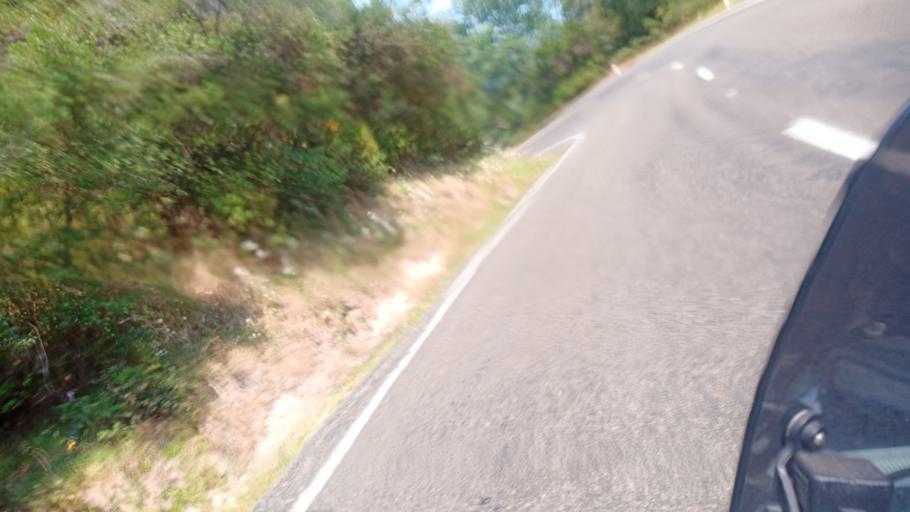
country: NZ
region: Bay of Plenty
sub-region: Opotiki District
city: Opotiki
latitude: -37.5936
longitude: 178.2254
